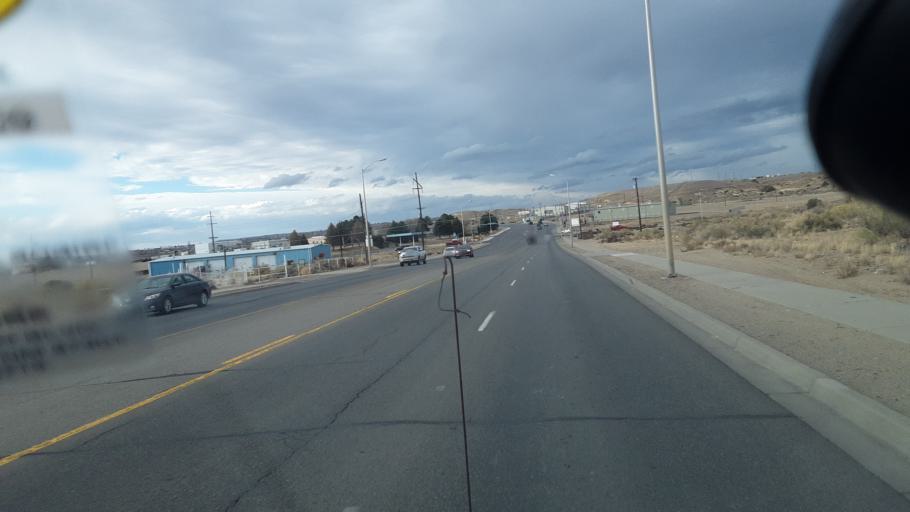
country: US
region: New Mexico
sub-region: San Juan County
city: Farmington
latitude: 36.7251
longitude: -108.1593
